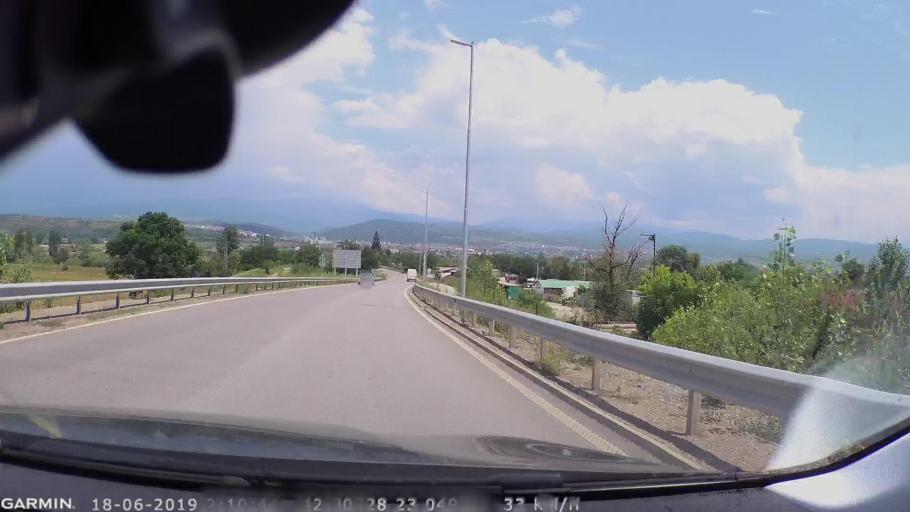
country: BG
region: Blagoevgrad
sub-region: Obshtina Blagoevgrad
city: Blagoevgrad
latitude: 41.9874
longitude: 23.0566
